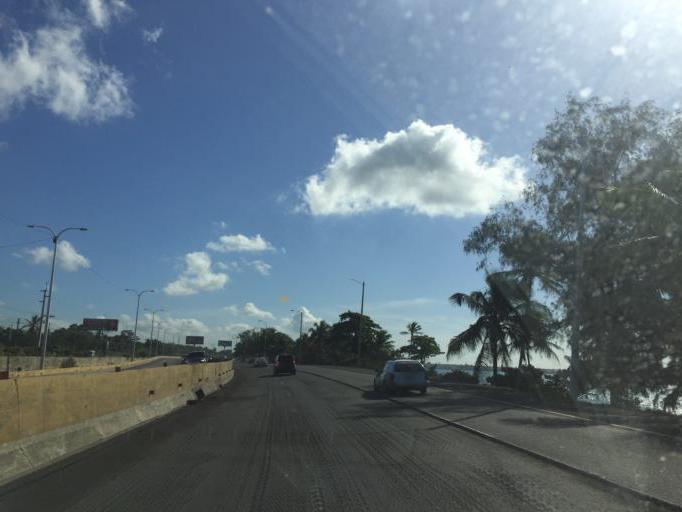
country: DO
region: Santo Domingo
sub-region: Santo Domingo
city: Boca Chica
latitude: 18.4555
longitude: -69.7021
